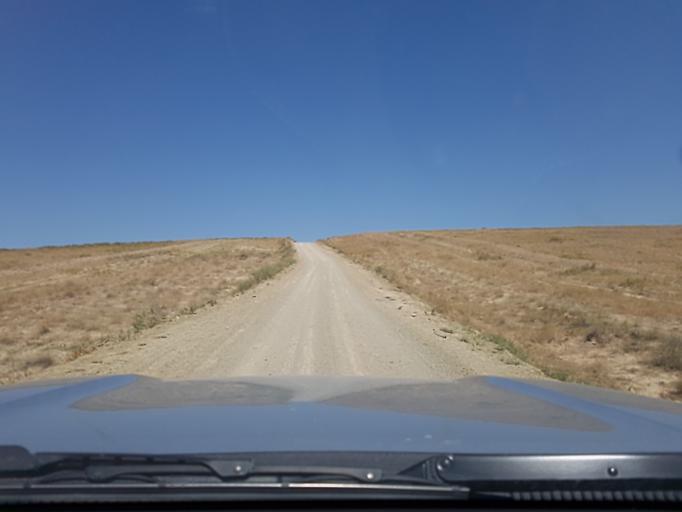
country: TM
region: Balkan
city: Magtymguly
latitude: 38.3436
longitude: 56.8170
